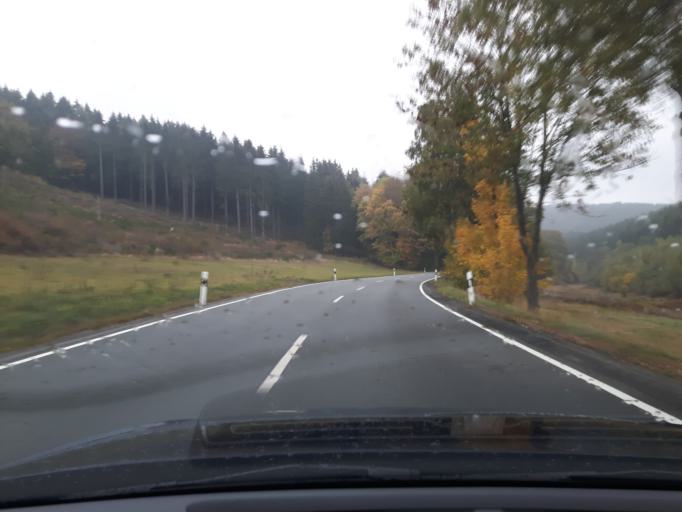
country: DE
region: North Rhine-Westphalia
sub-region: Regierungsbezirk Arnsberg
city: Bad Berleburg
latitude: 50.9994
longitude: 8.3990
